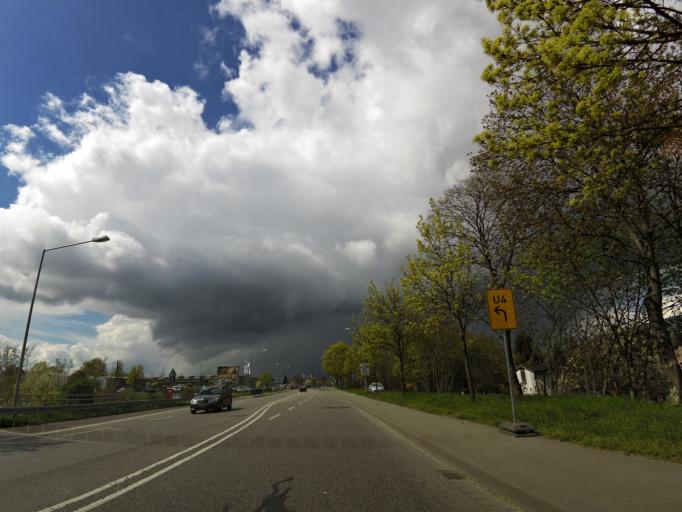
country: DE
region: Saxony-Anhalt
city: Biederitz
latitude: 52.1315
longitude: 11.6866
